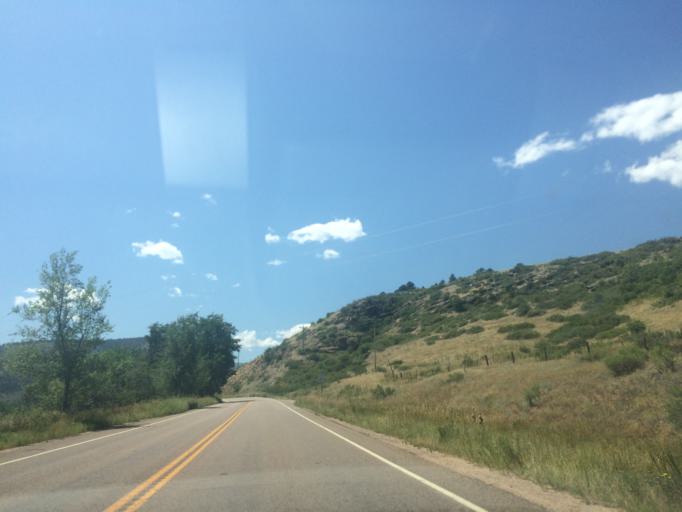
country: US
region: Colorado
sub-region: Boulder County
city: Lyons
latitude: 40.2176
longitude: -105.2741
